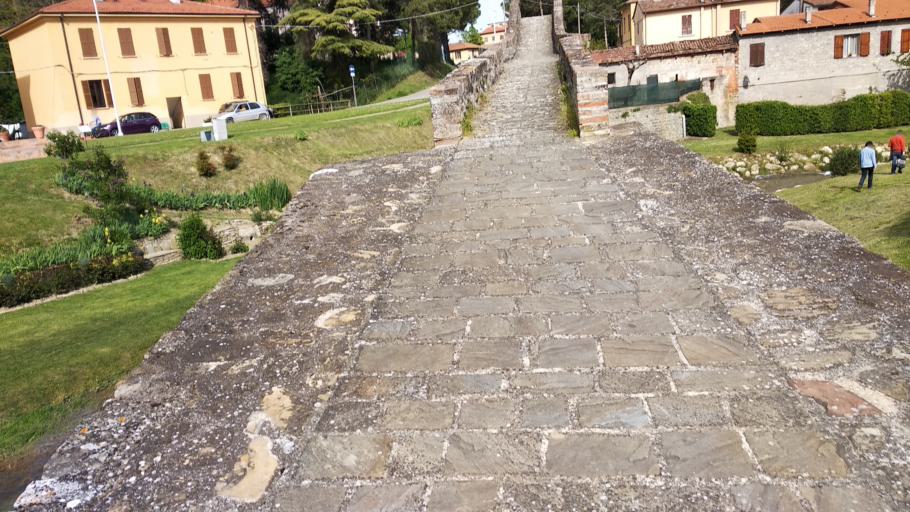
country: IT
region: Emilia-Romagna
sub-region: Forli-Cesena
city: Modigliana
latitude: 44.1601
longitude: 11.7918
